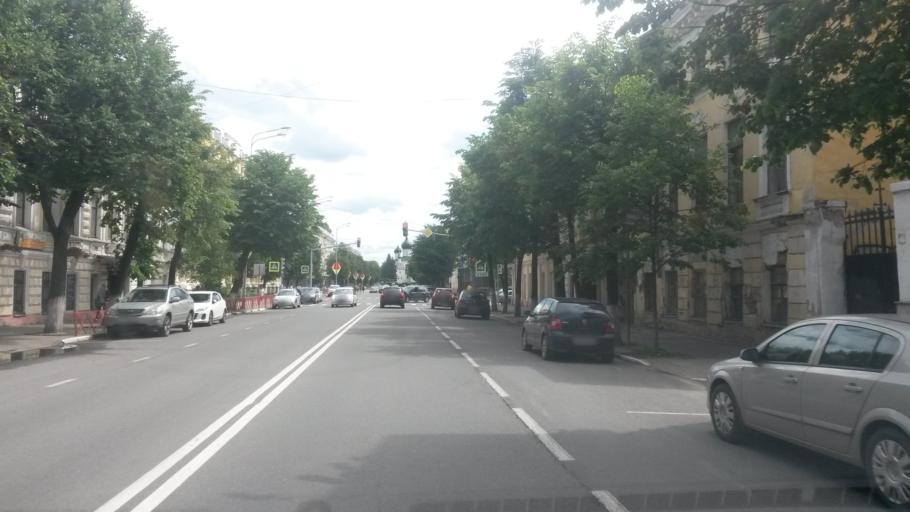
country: RU
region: Jaroslavl
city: Yaroslavl
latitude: 57.6306
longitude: 39.8897
